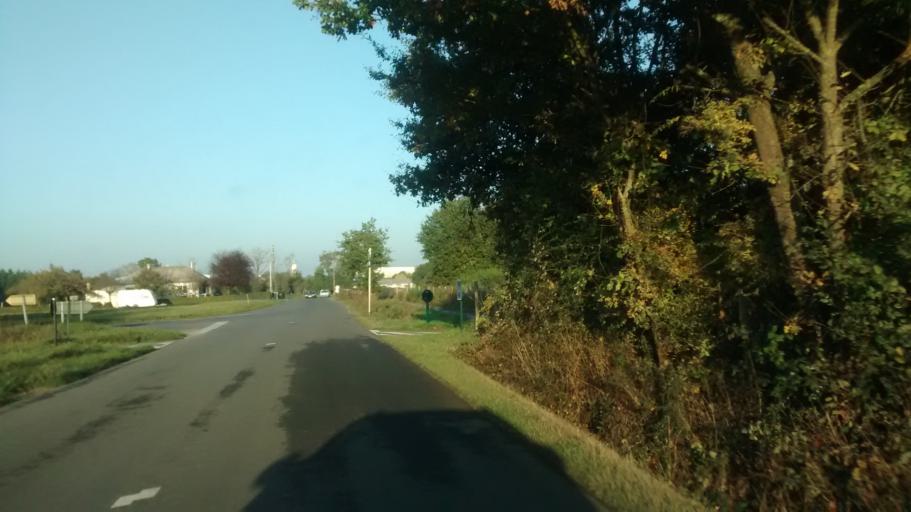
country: FR
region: Brittany
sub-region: Departement d'Ille-et-Vilaine
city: La Chapelle-Thouarault
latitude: 48.1196
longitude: -1.8357
